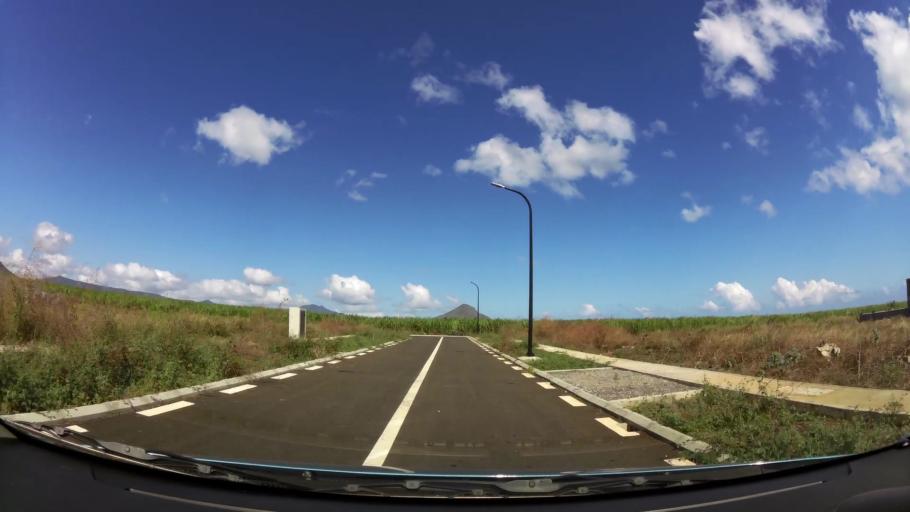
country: MU
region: Black River
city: Cascavelle
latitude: -20.2829
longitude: 57.3874
